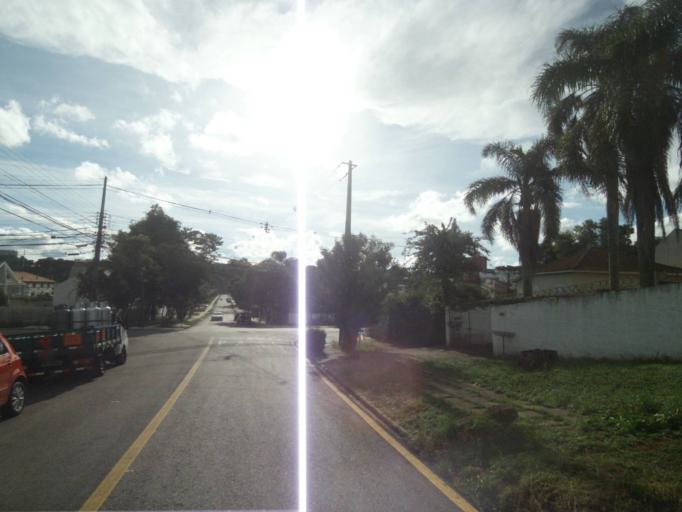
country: BR
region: Parana
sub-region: Curitiba
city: Curitiba
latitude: -25.4427
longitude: -49.3119
